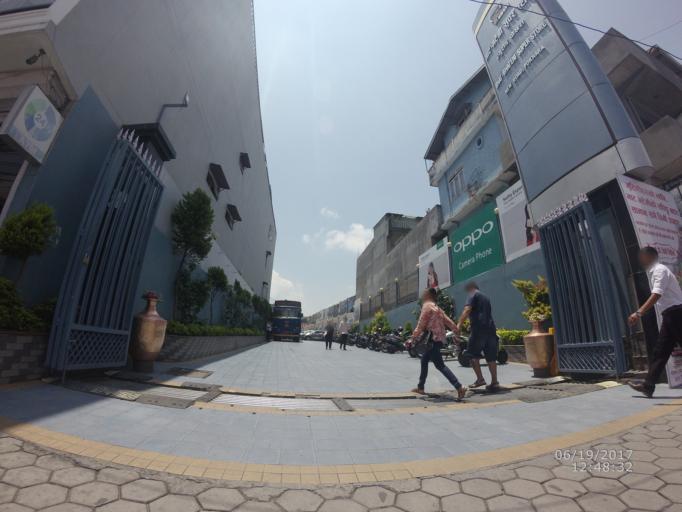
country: NP
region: Western Region
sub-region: Gandaki Zone
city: Pokhara
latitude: 28.2207
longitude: 83.9870
